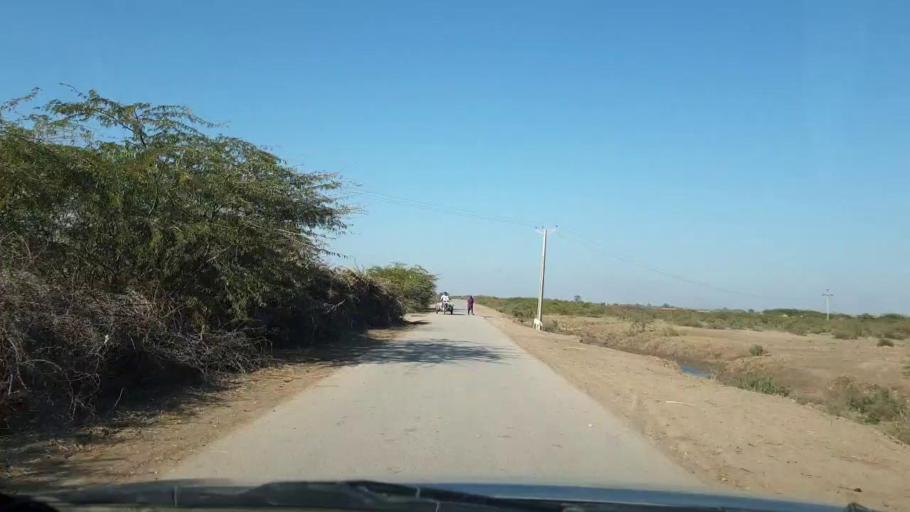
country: PK
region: Sindh
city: Jhol
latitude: 25.8351
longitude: 68.9513
